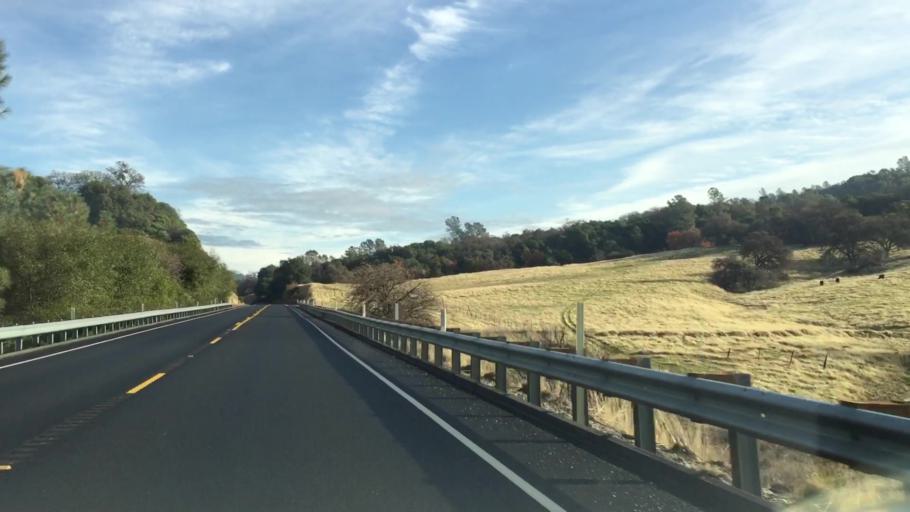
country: US
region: California
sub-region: Butte County
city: Oroville
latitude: 39.6384
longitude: -121.5766
